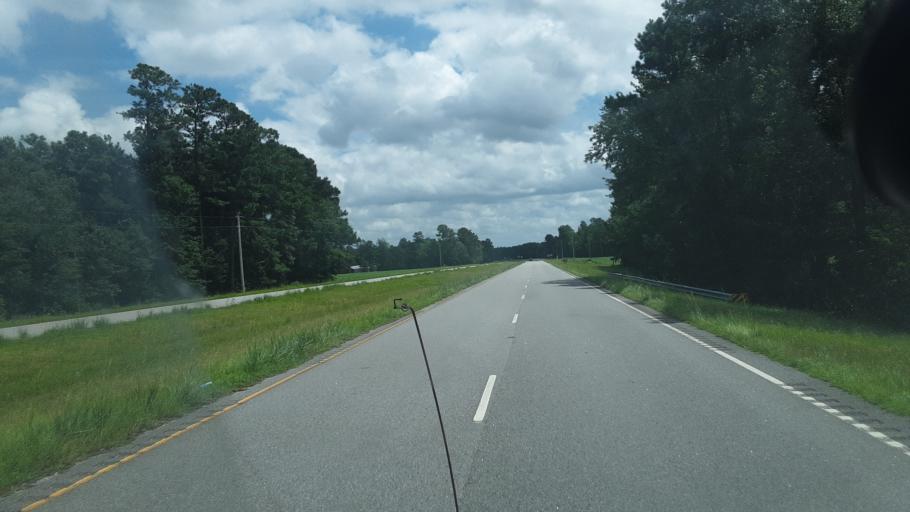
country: US
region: South Carolina
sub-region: Horry County
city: Loris
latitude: 34.1020
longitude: -78.9254
